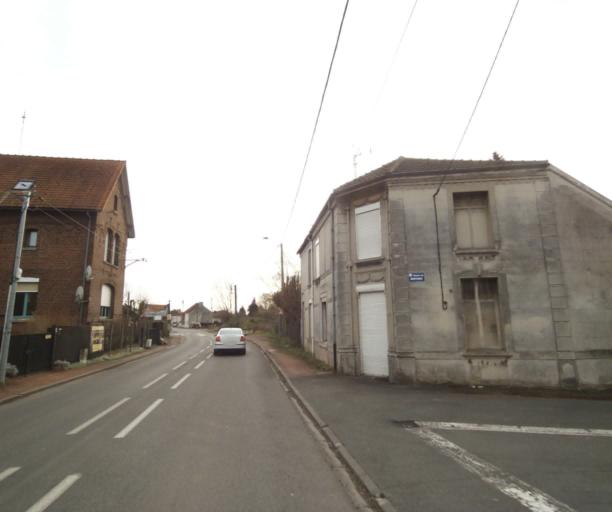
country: FR
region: Nord-Pas-de-Calais
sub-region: Departement du Nord
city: Hergnies
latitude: 50.4666
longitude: 3.5465
